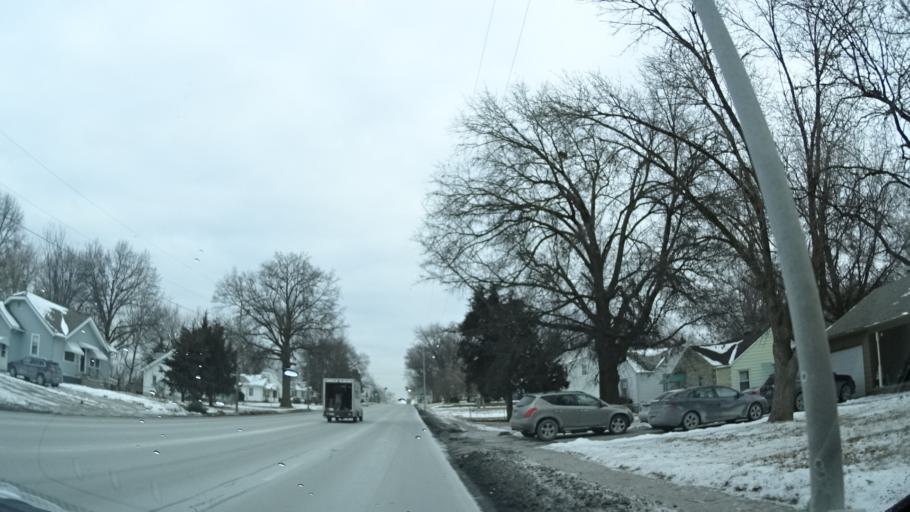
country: US
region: Nebraska
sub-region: Douglas County
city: Omaha
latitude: 41.2322
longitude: -95.9758
